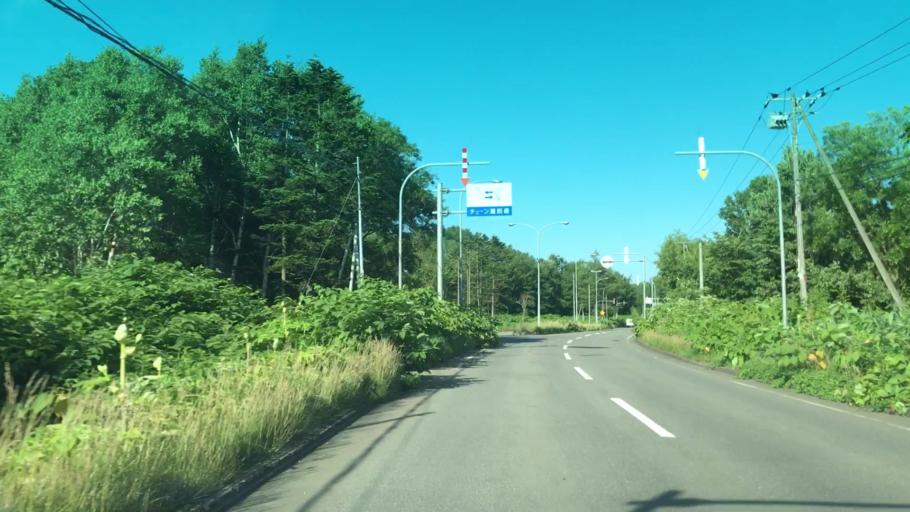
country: JP
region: Hokkaido
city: Otaru
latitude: 43.0883
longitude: 140.9255
